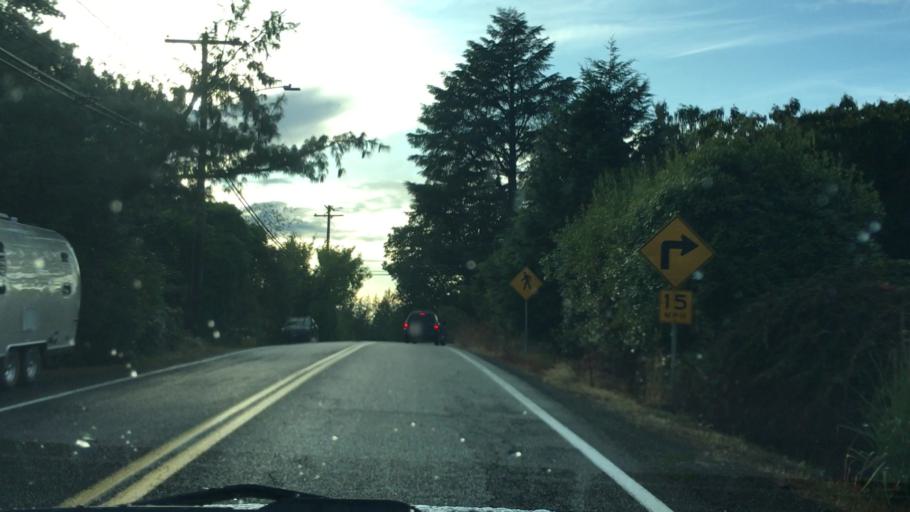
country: US
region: Oregon
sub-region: Multnomah County
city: Portland
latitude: 45.4852
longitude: -122.7095
